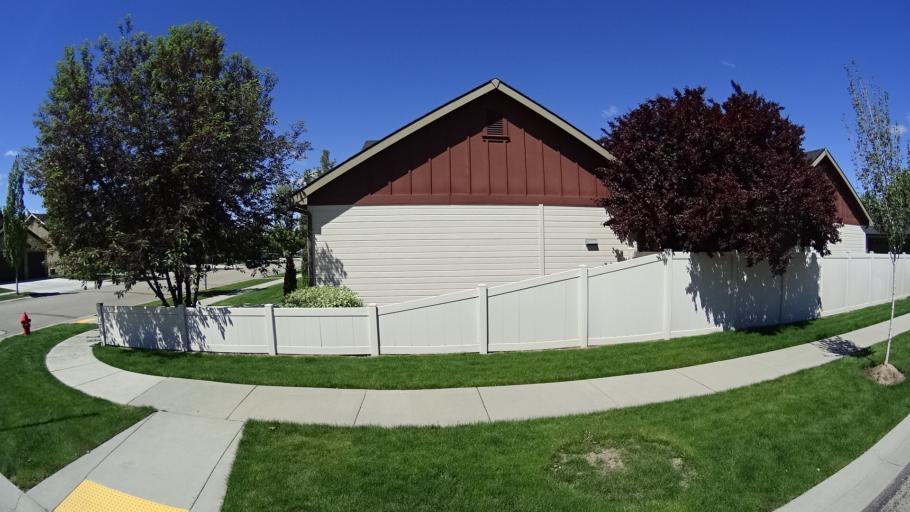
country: US
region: Idaho
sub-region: Ada County
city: Eagle
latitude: 43.6598
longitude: -116.3825
